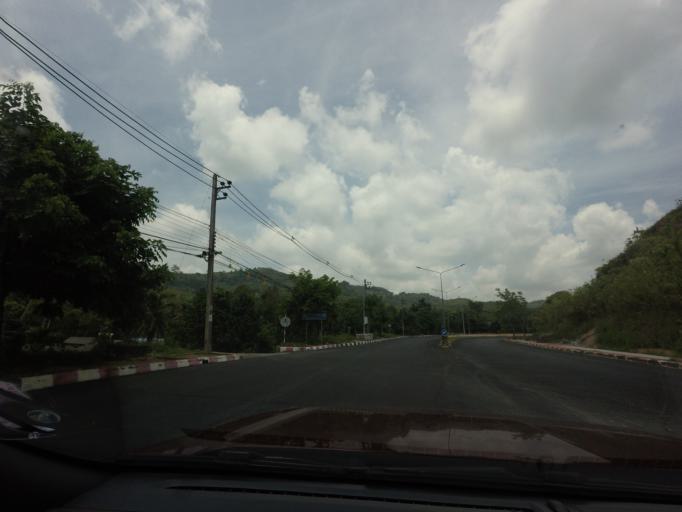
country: TH
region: Yala
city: Betong
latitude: 5.7532
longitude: 101.0439
